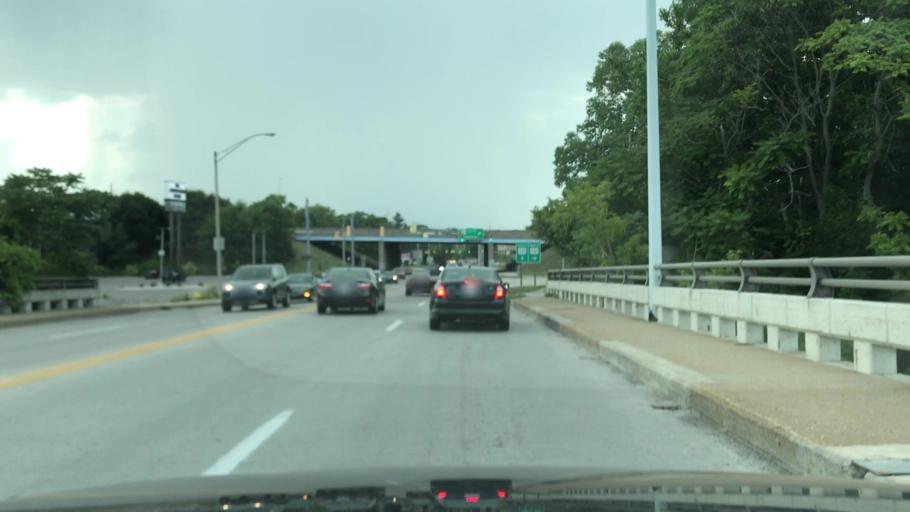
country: US
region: Michigan
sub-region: Kent County
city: Grand Rapids
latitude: 42.9956
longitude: -85.6741
